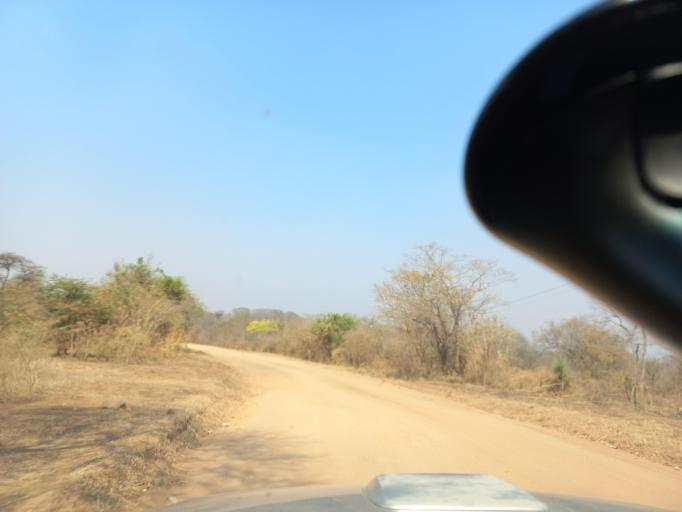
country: ZW
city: Chirundu
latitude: -15.9259
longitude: 28.8842
